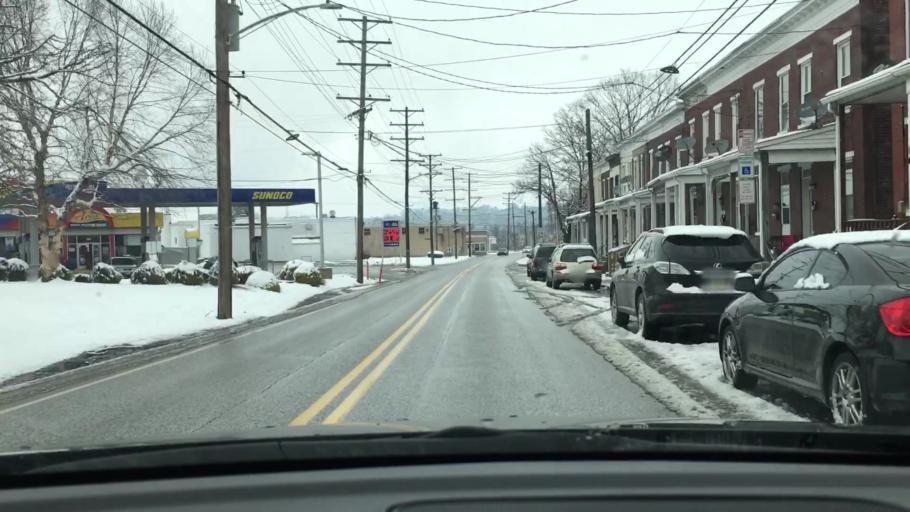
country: US
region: Pennsylvania
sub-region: York County
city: York
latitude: 39.9718
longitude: -76.7130
